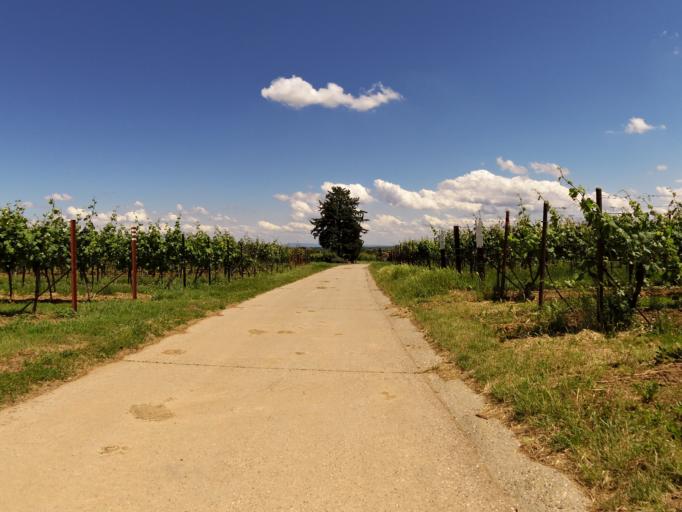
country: DE
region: Rheinland-Pfalz
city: Edesheim
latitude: 49.2632
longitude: 8.1223
